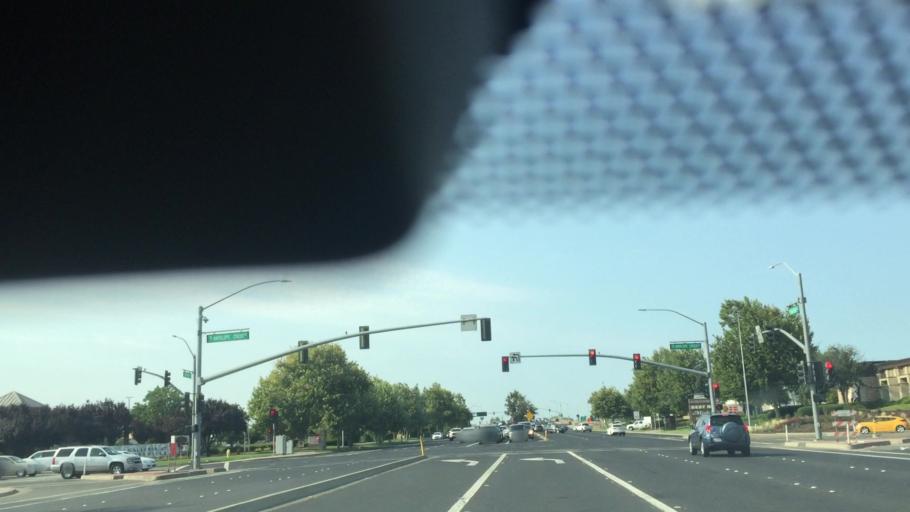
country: US
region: California
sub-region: Placer County
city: Roseville
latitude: 38.7715
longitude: -121.2658
